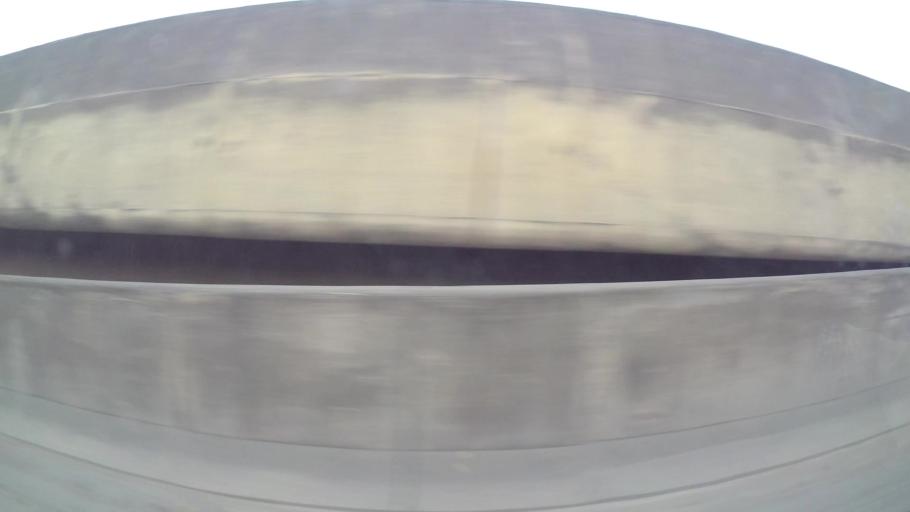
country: VN
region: Ha Noi
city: Thanh Xuan
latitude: 20.9879
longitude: 105.8057
